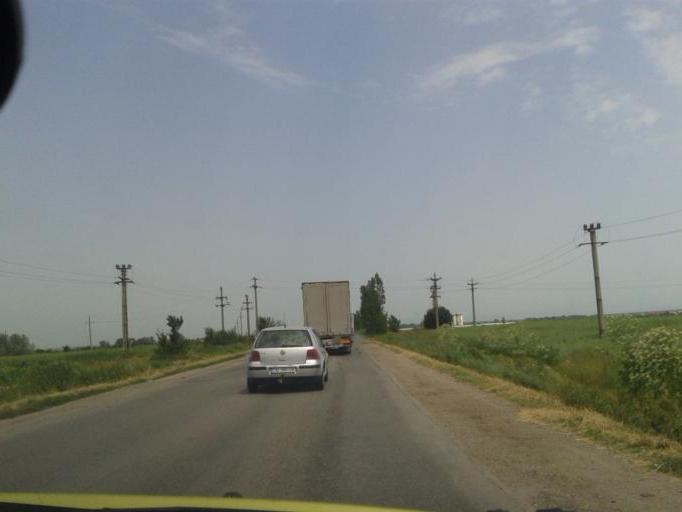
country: RO
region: Dambovita
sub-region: Oras Gaesti
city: Gaesti
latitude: 44.6913
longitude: 25.3128
